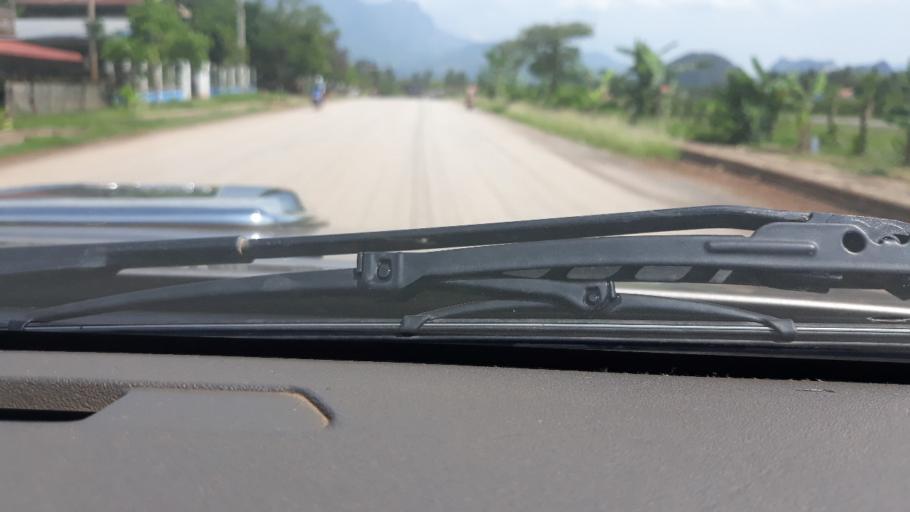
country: LA
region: Xiagnabouli
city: Sainyabuli
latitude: 19.2413
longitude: 101.7109
